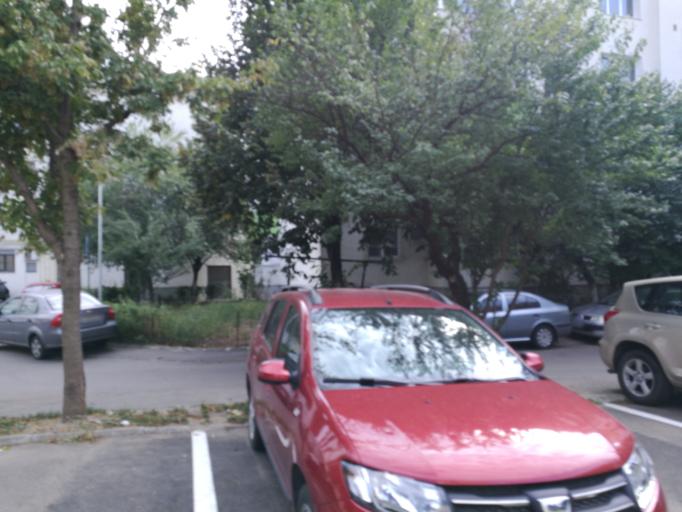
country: RO
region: Bucuresti
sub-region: Municipiul Bucuresti
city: Bucharest
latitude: 44.4800
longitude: 26.0977
